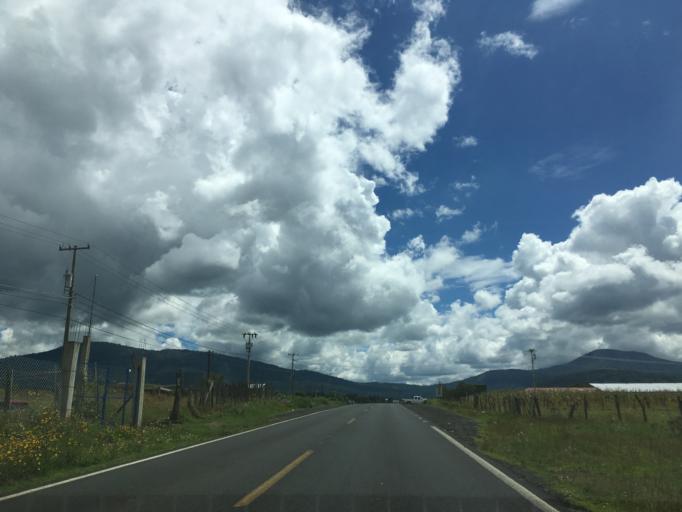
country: MX
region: Michoacan
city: Cheran
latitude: 19.6673
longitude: -101.9431
